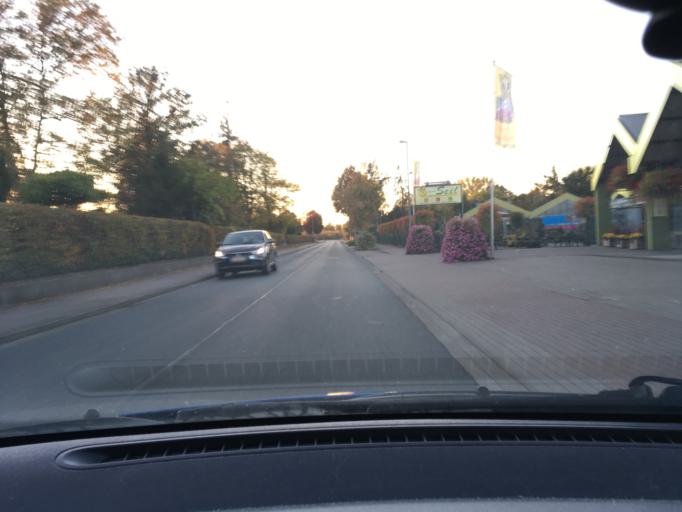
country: DE
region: Lower Saxony
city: Bleckede
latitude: 53.2973
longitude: 10.7195
